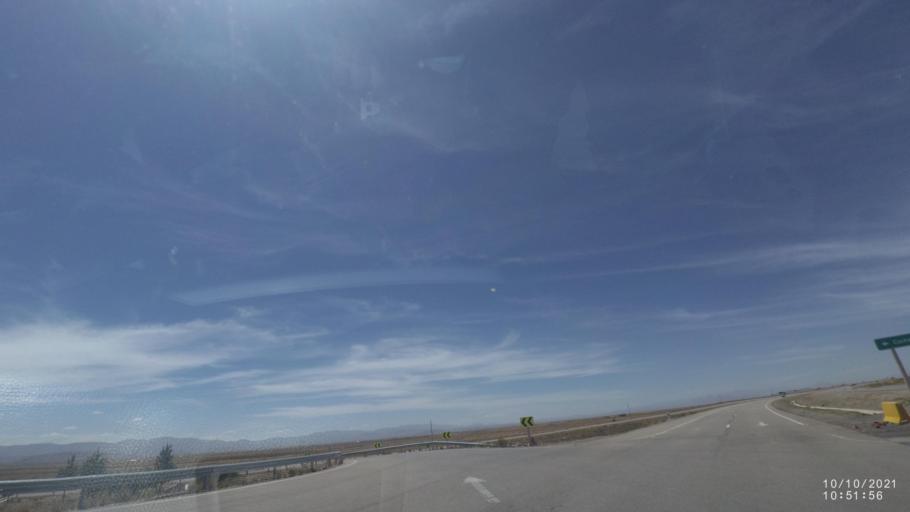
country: BO
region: La Paz
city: Colquiri
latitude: -17.6571
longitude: -67.2079
